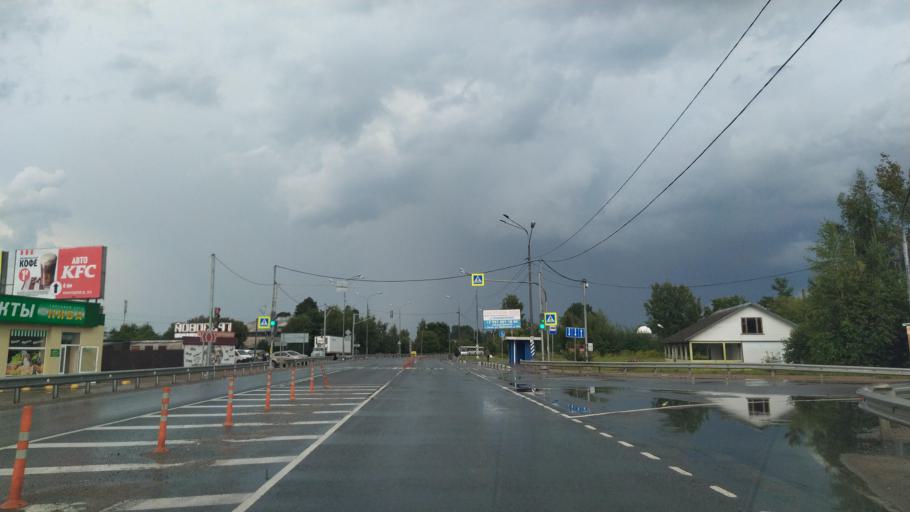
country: RU
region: Pskov
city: Pskov
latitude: 57.7443
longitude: 28.3704
